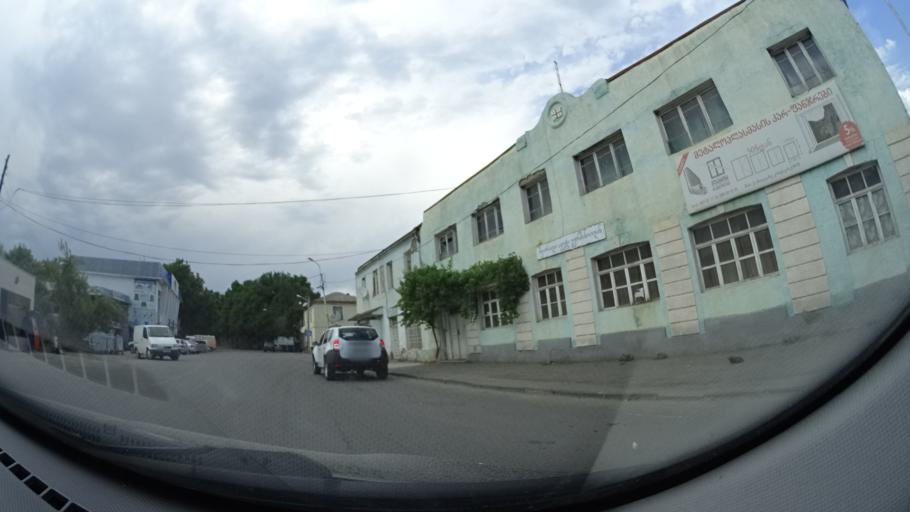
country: GE
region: Samtskhe-Javakheti
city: Aspindza
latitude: 41.5762
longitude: 43.2477
